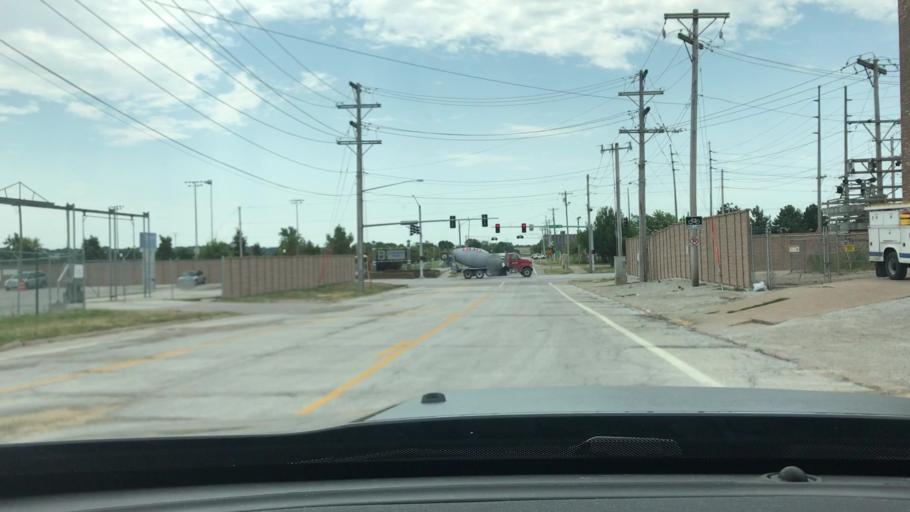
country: US
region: Iowa
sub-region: Scott County
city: Davenport
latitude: 41.5209
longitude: -90.5909
